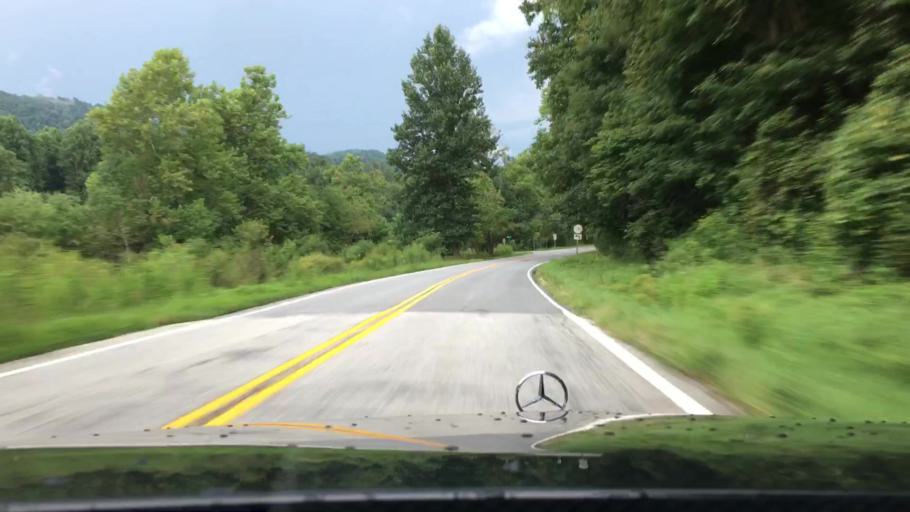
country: US
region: Virginia
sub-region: Nelson County
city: Lovingston
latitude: 37.8182
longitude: -78.9363
